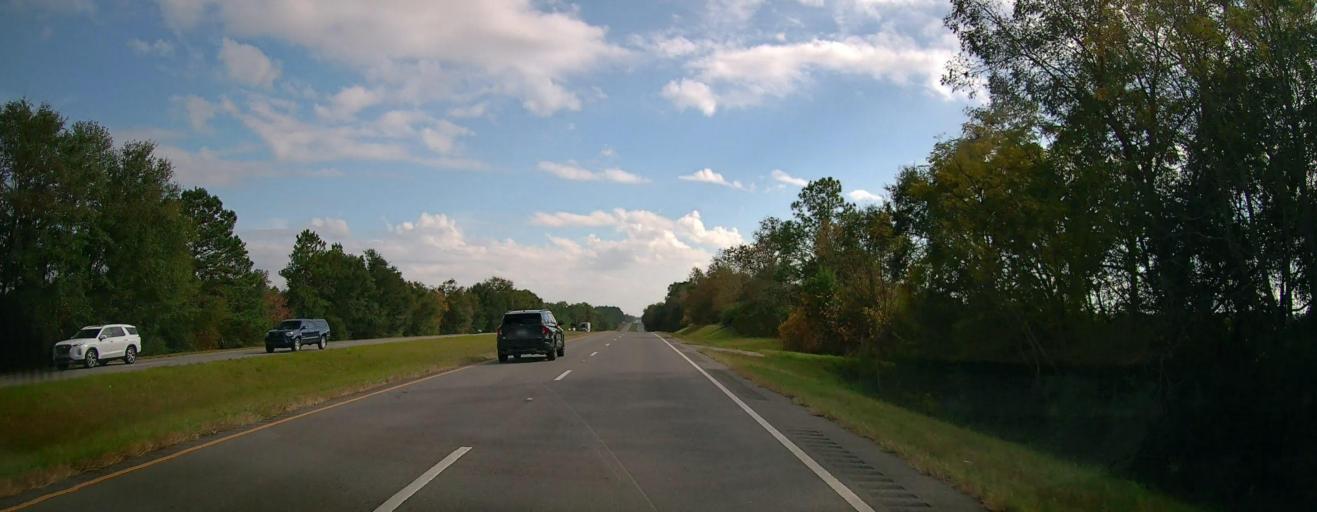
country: US
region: Georgia
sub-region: Thomas County
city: Meigs
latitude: 30.9907
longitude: -84.0436
